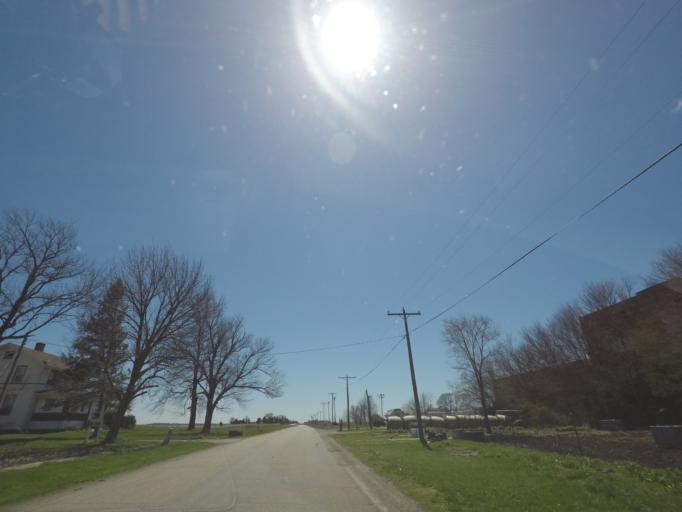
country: US
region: Illinois
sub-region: Logan County
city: Atlanta
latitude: 40.1397
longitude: -89.1932
